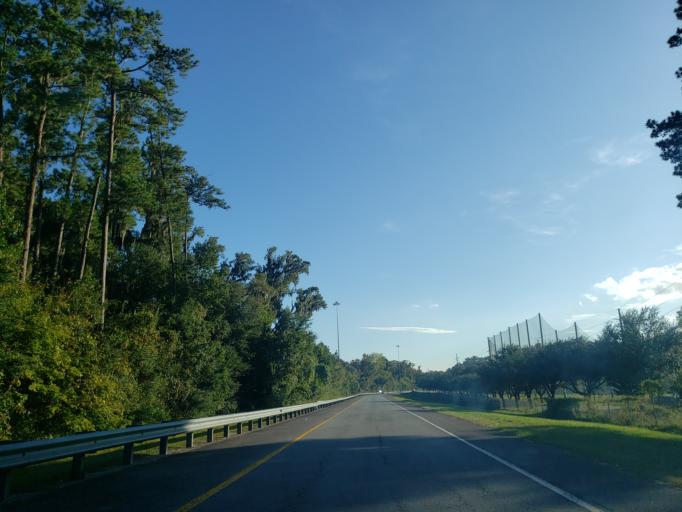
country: US
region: Georgia
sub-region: Chatham County
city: Isle of Hope
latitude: 32.0066
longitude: -81.0803
